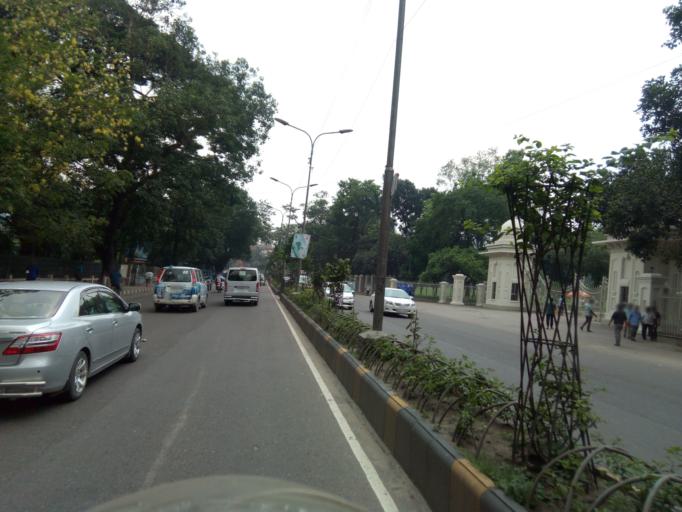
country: BD
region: Dhaka
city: Paltan
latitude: 23.7317
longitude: 90.4047
